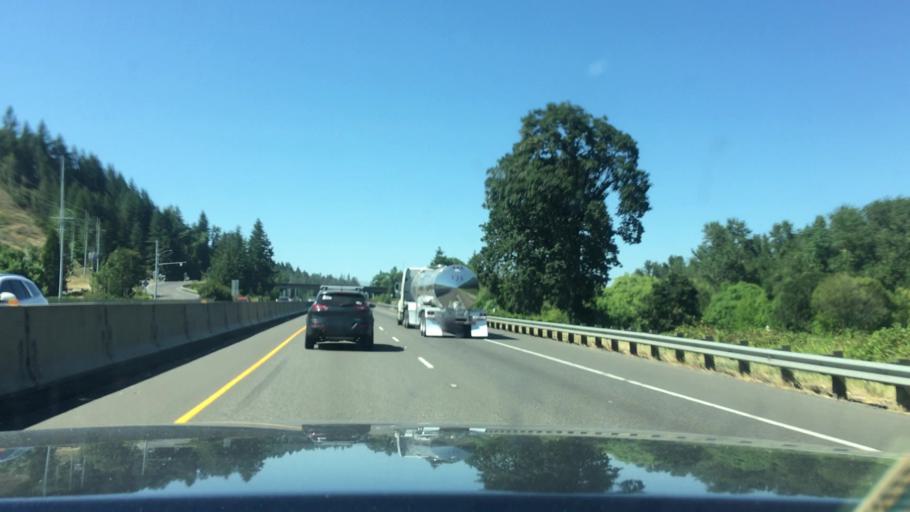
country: US
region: Oregon
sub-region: Lane County
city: Springfield
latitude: 44.0190
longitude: -123.0257
